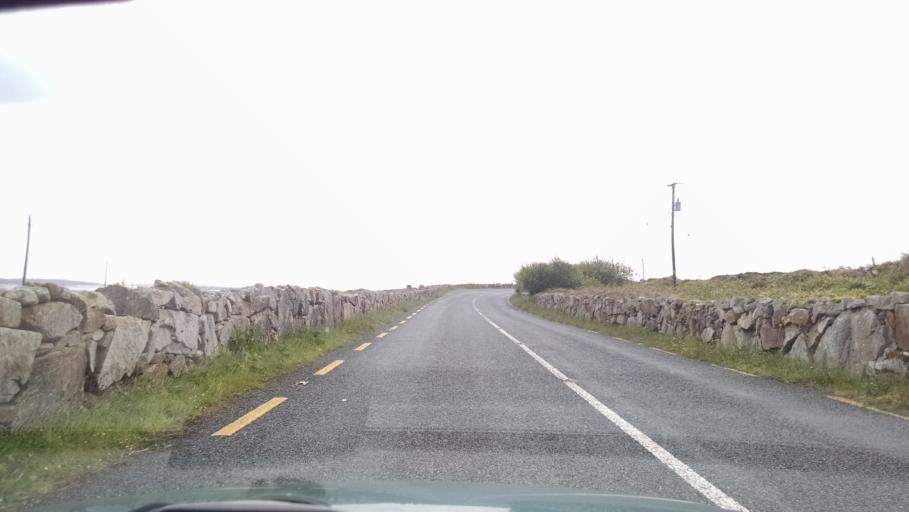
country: IE
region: Connaught
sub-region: County Galway
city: Clifden
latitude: 53.3127
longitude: -9.7329
